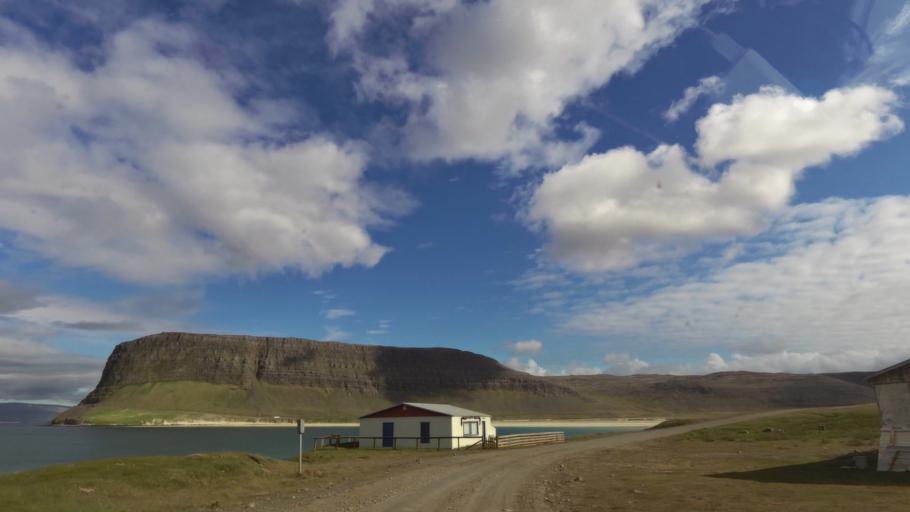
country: IS
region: West
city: Olafsvik
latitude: 65.5912
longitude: -24.1239
